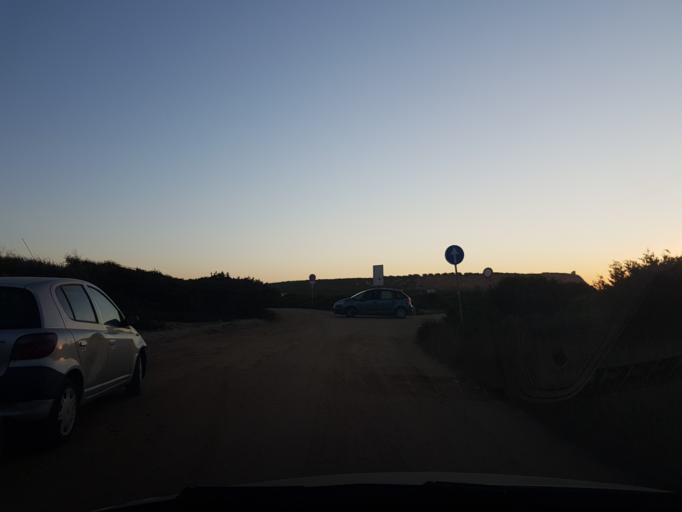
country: IT
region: Sardinia
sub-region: Provincia di Oristano
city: Riola Sardo
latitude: 40.0433
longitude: 8.4007
